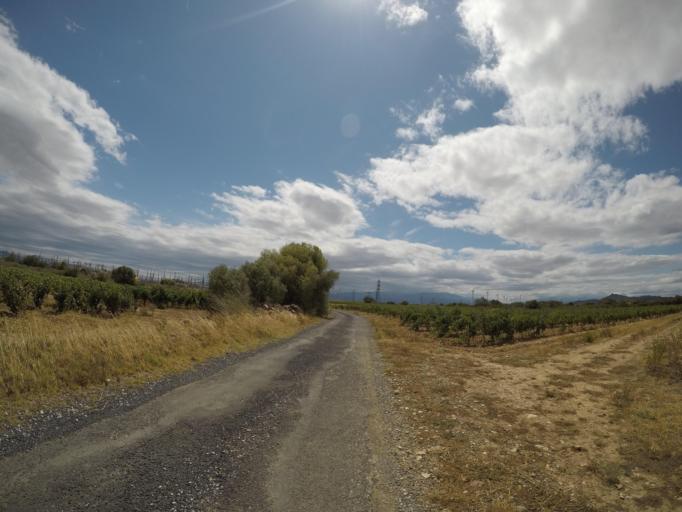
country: FR
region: Languedoc-Roussillon
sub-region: Departement des Pyrenees-Orientales
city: Baixas
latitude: 42.7365
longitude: 2.8025
